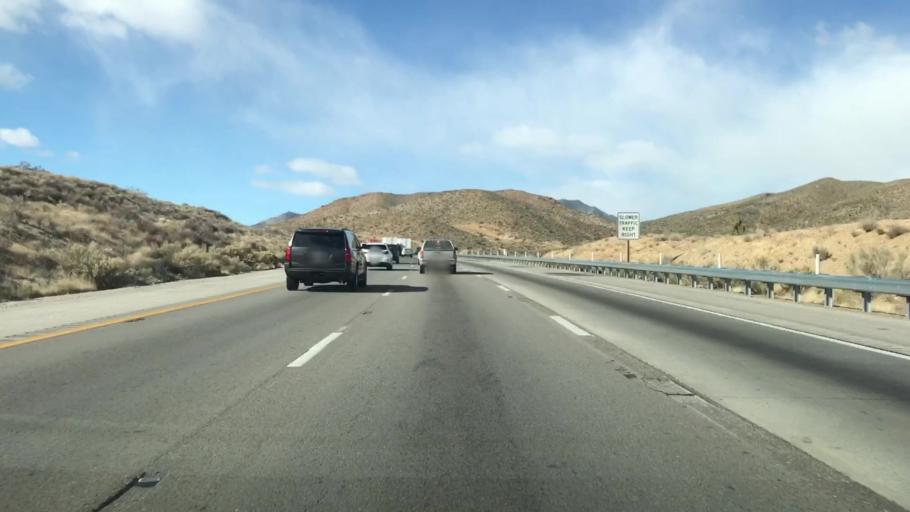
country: US
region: Nevada
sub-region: Clark County
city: Sandy Valley
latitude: 35.4666
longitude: -115.4846
